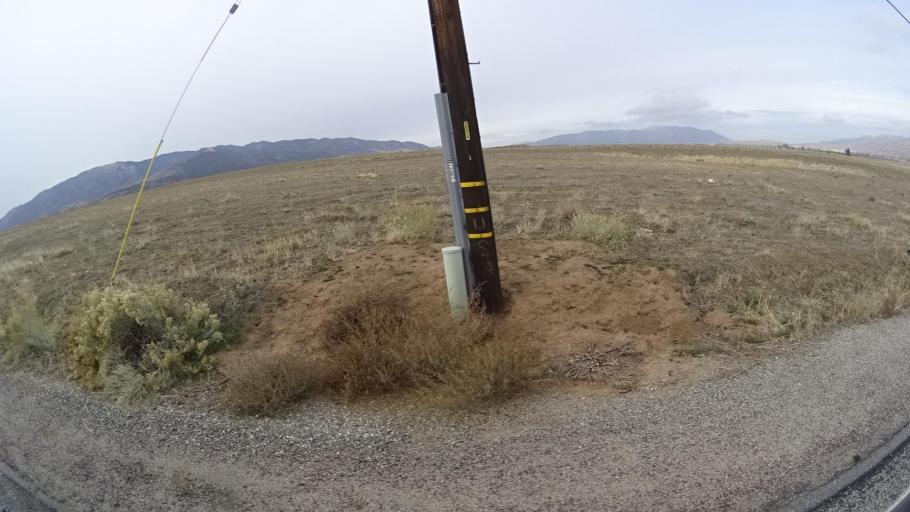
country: US
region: California
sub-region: Kern County
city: Tehachapi
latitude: 35.0995
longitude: -118.3968
